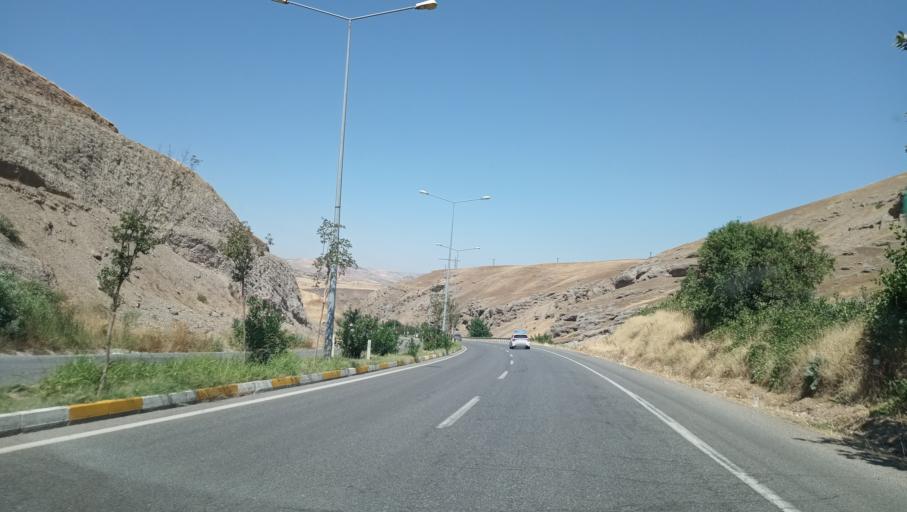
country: TR
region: Siirt
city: Civankan
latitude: 37.9483
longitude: 41.8732
